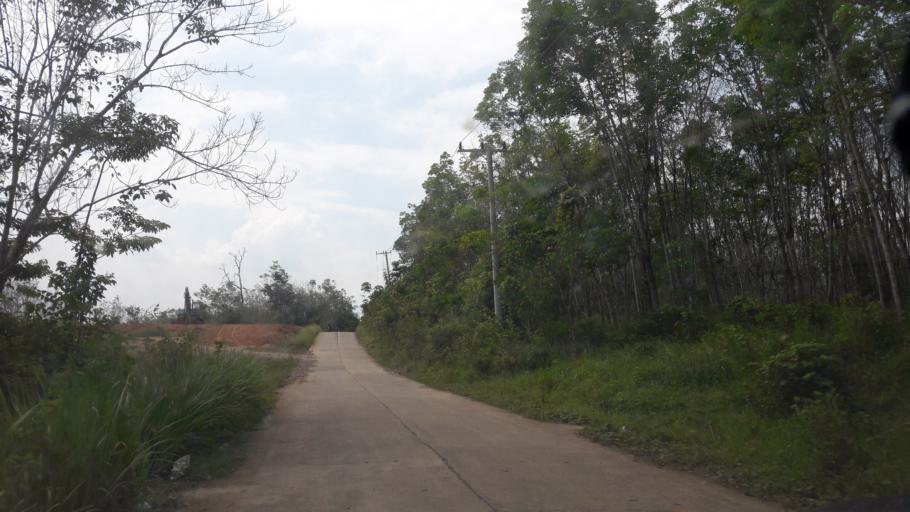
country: ID
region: South Sumatra
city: Gunungmegang Dalam
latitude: -3.2992
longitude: 103.8609
